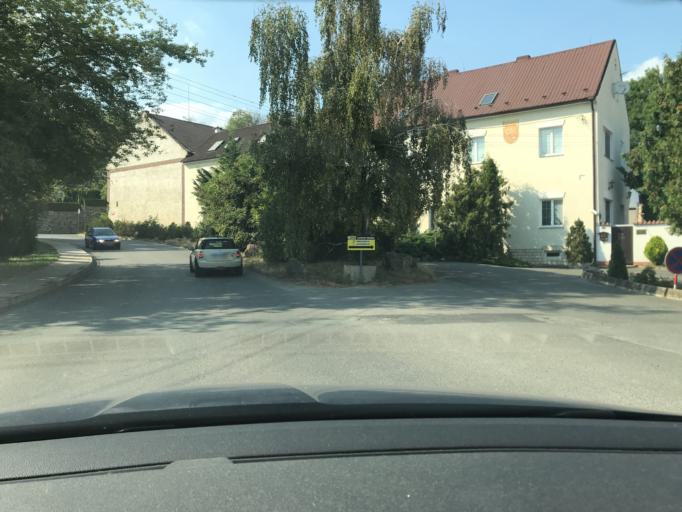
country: CZ
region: Central Bohemia
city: Velke Prilepy
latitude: 50.1603
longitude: 14.3145
